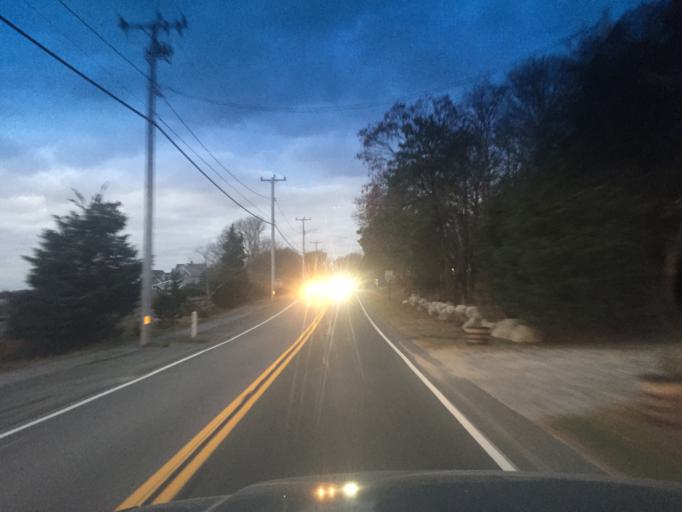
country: US
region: Massachusetts
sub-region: Barnstable County
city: Monument Beach
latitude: 41.7149
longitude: -70.6145
